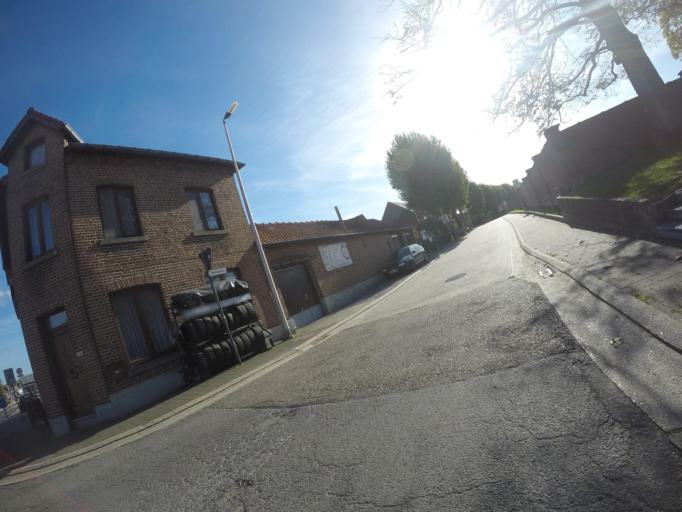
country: BE
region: Flanders
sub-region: Provincie Limburg
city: Diepenbeek
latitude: 50.9065
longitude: 5.4276
